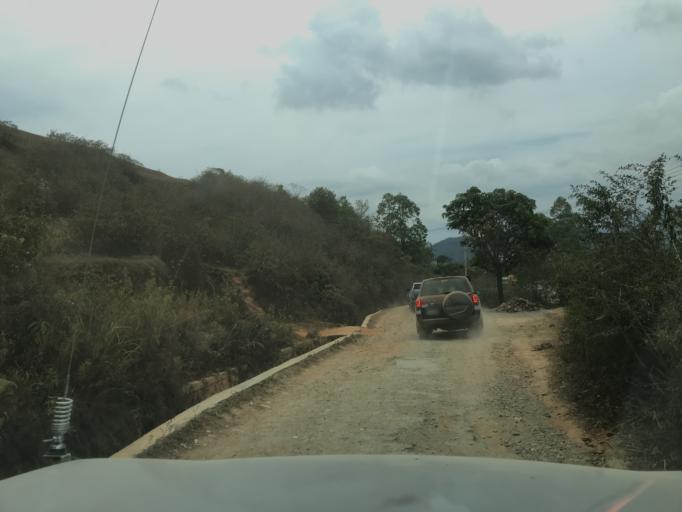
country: TL
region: Ermera
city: Gleno
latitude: -8.8380
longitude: 125.4363
